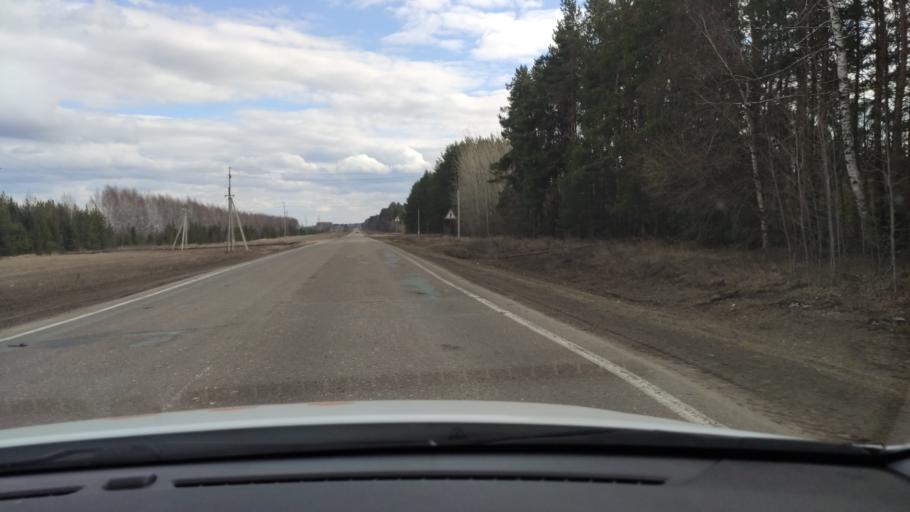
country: RU
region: Tatarstan
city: Vysokaya Gora
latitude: 56.0527
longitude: 49.2117
